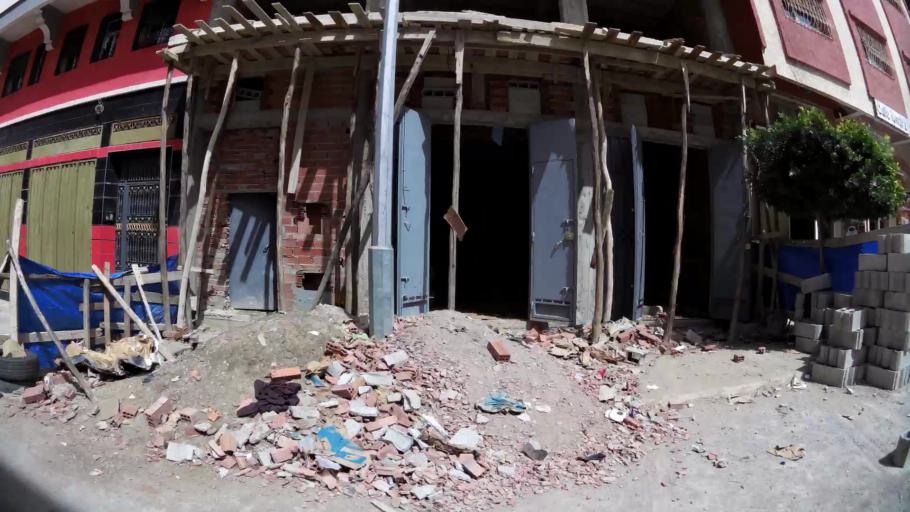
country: MA
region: Tanger-Tetouan
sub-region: Tanger-Assilah
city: Tangier
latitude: 35.7460
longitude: -5.8349
